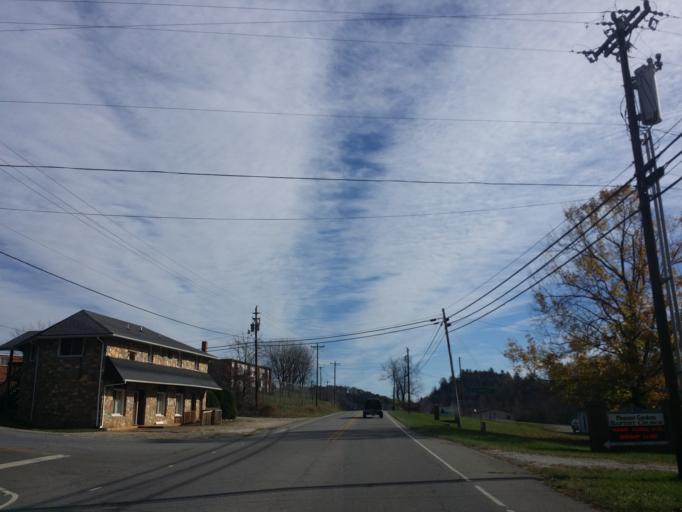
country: US
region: North Carolina
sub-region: McDowell County
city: West Marion
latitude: 35.6905
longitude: -82.0729
